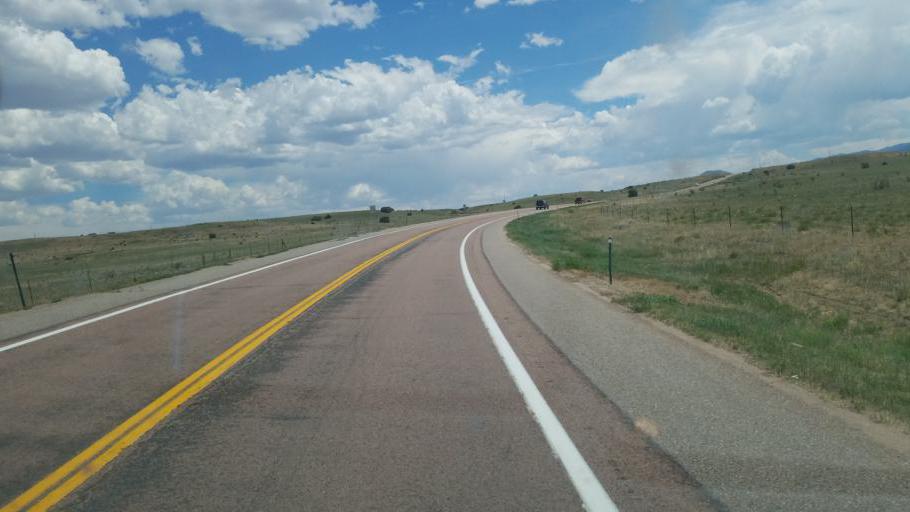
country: US
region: Colorado
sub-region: Fremont County
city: Florence
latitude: 38.2988
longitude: -105.0890
